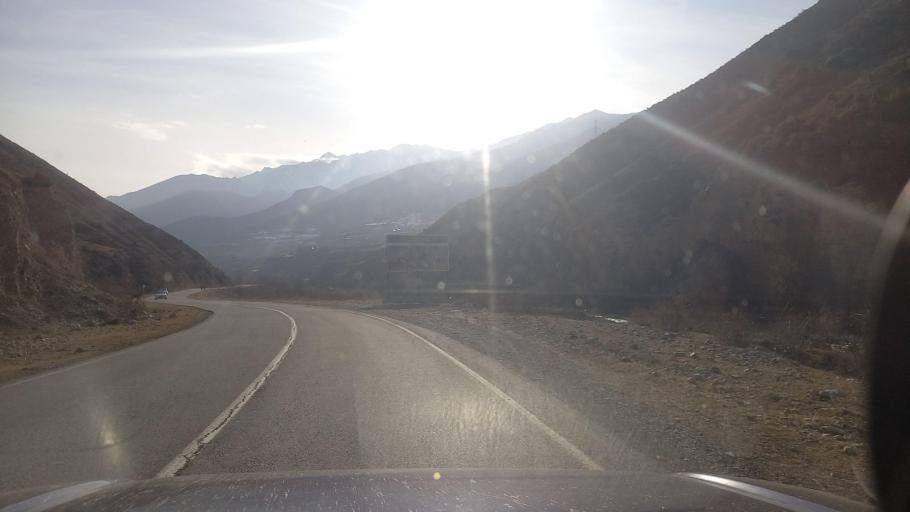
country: RU
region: Ingushetiya
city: Dzhayrakh
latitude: 42.8410
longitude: 44.6565
